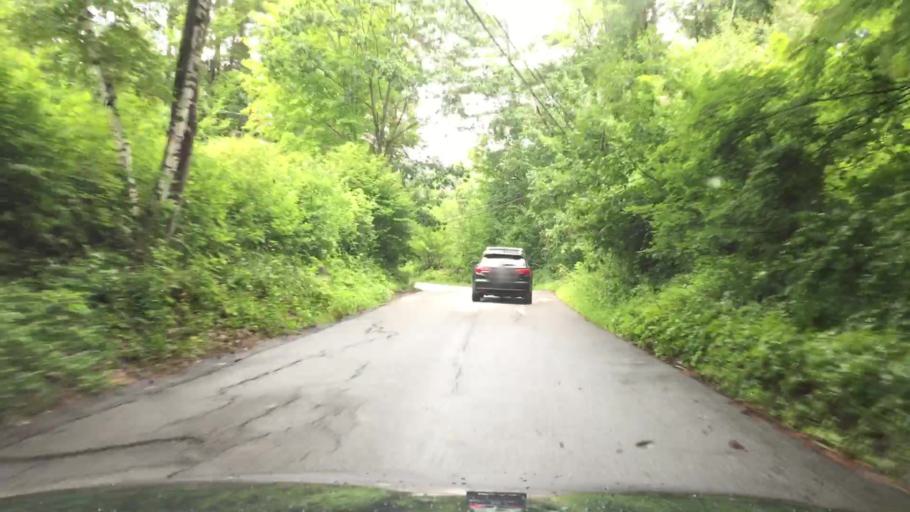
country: US
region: New Hampshire
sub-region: Grafton County
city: Holderness
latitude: 43.7246
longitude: -71.5685
